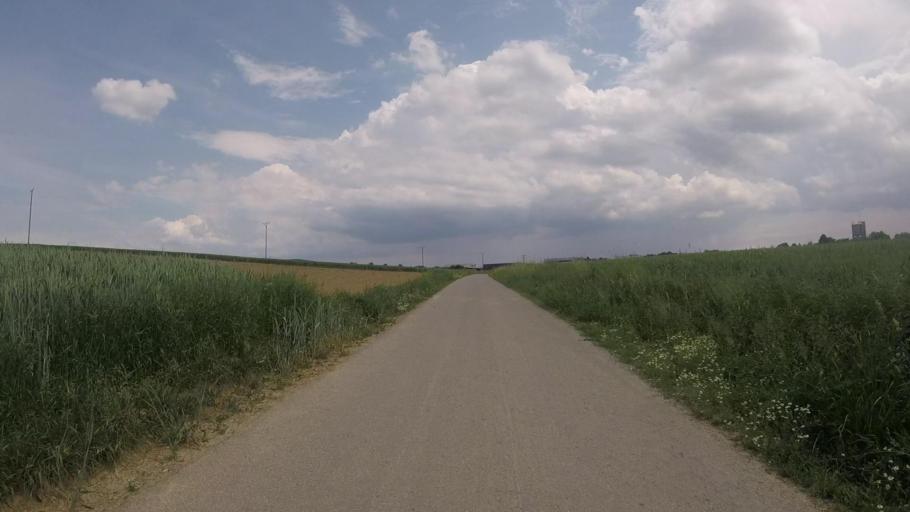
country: DE
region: Baden-Wuerttemberg
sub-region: Regierungsbezirk Stuttgart
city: Aspach
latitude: 48.9607
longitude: 9.4171
